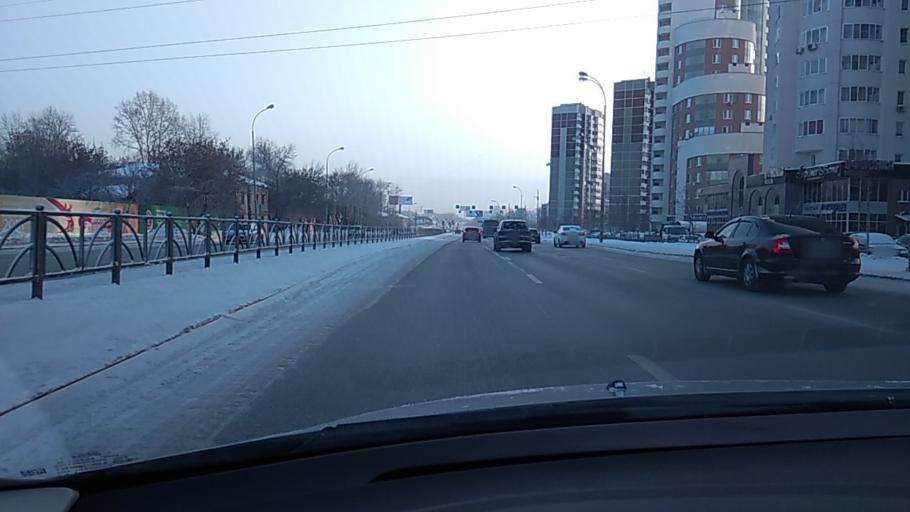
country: RU
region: Sverdlovsk
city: Yekaterinburg
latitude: 56.8035
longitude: 60.6340
